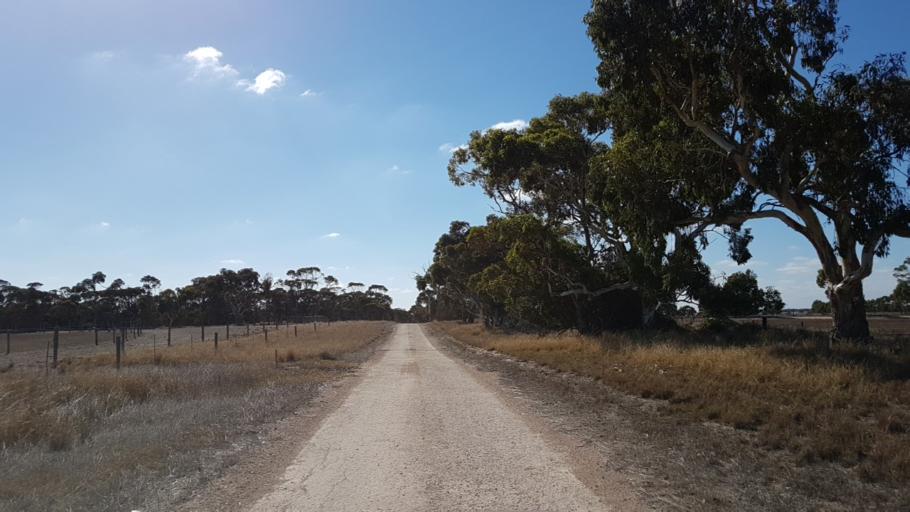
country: AU
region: South Australia
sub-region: Alexandrina
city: Goolwa
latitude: -35.3803
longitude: 138.8284
